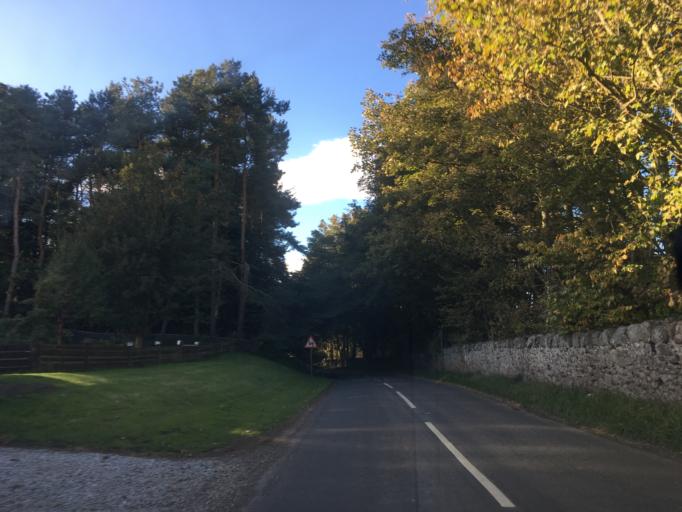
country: GB
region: Scotland
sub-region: East Lothian
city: Pencaitland
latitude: 55.8669
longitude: -2.8871
